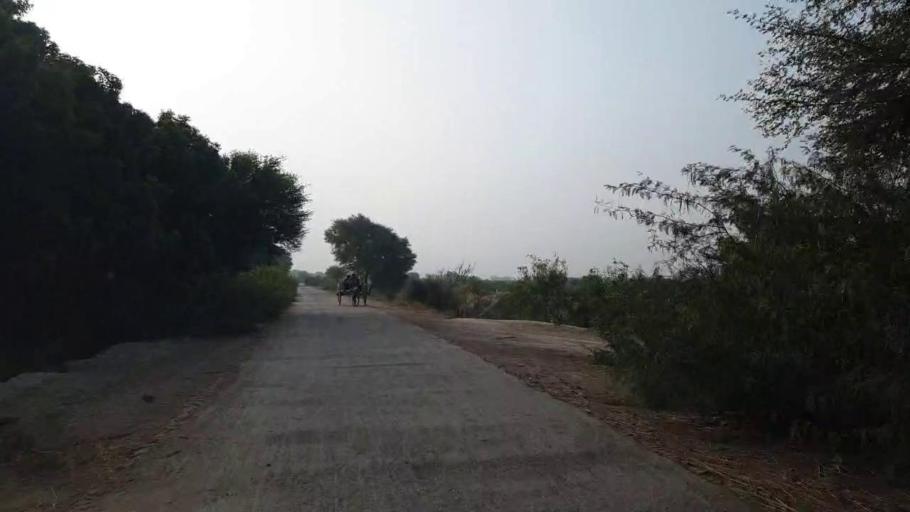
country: PK
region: Sindh
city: Tando Muhammad Khan
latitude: 25.1720
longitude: 68.6066
